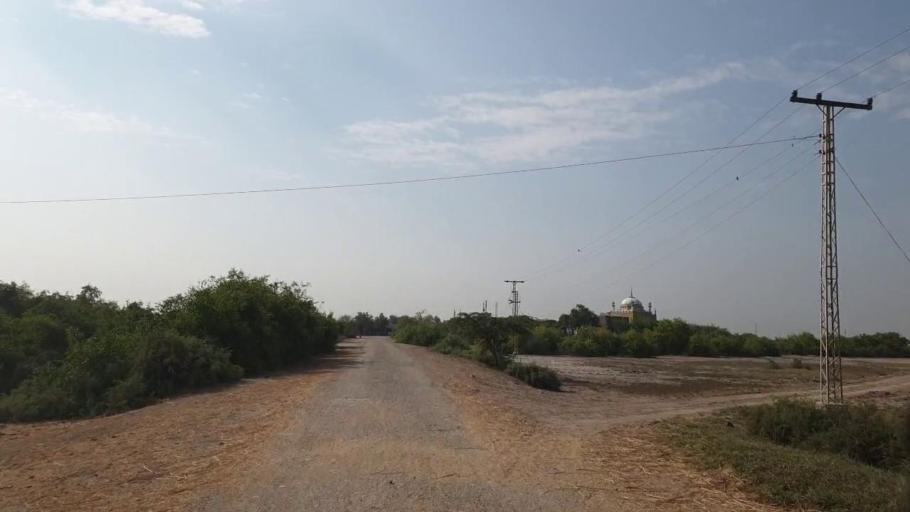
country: PK
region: Sindh
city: Tando Muhammad Khan
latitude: 25.0593
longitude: 68.4135
